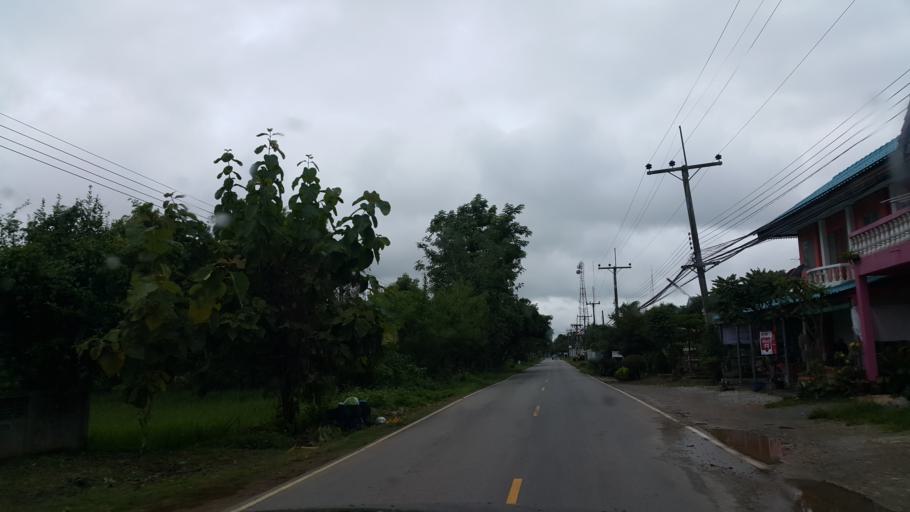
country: TH
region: Phayao
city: Chiang Kham
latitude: 19.5284
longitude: 100.3143
